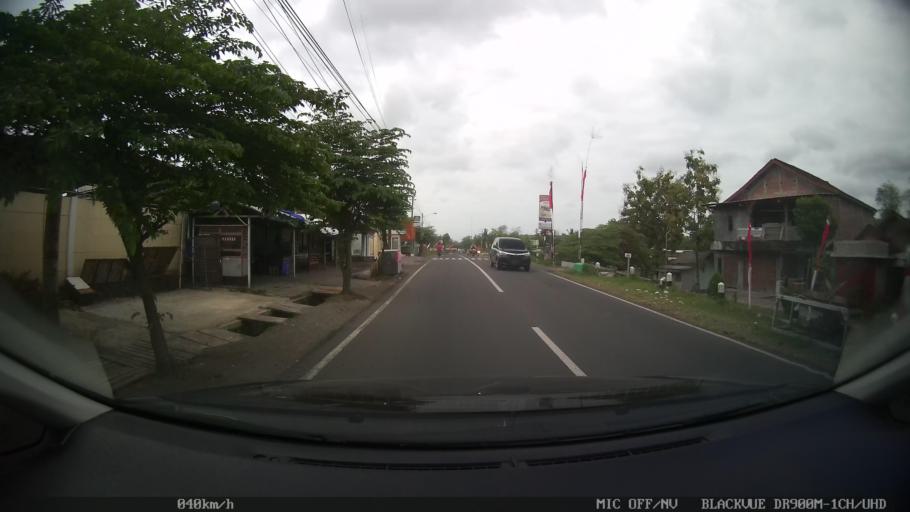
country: ID
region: Daerah Istimewa Yogyakarta
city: Sewon
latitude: -7.8483
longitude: 110.4377
